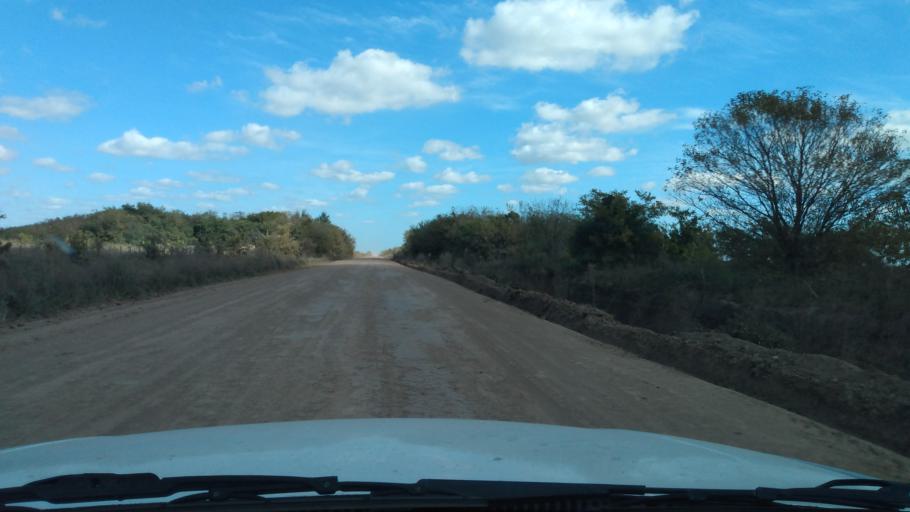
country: AR
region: Buenos Aires
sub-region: Partido de Navarro
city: Navarro
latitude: -35.0305
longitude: -59.4500
